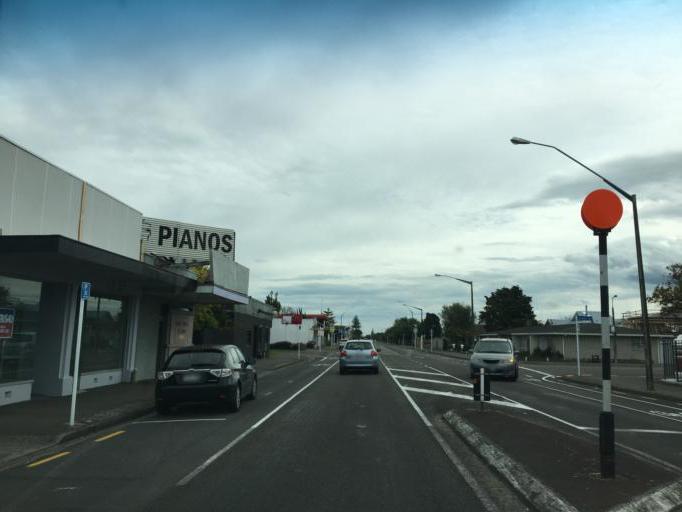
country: NZ
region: Manawatu-Wanganui
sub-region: Palmerston North City
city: Palmerston North
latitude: -40.3513
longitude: 175.6033
